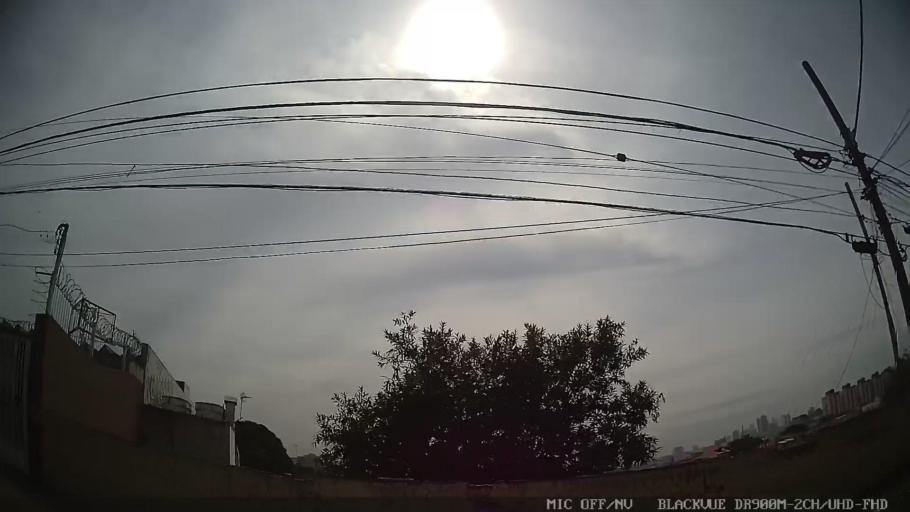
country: BR
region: Sao Paulo
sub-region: Guarulhos
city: Guarulhos
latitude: -23.5273
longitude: -46.5477
